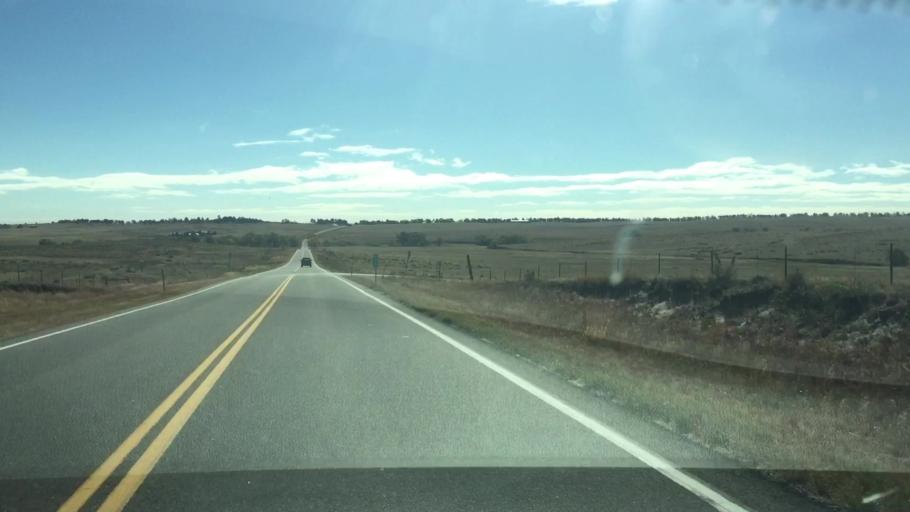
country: US
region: Colorado
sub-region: Elbert County
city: Kiowa
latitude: 39.3255
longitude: -104.3953
